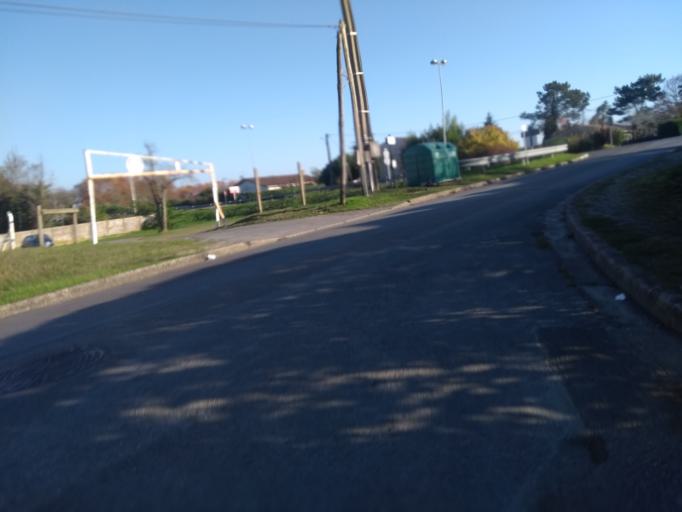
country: FR
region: Aquitaine
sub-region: Departement de la Gironde
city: Cadaujac
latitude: 44.7526
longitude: -0.5406
